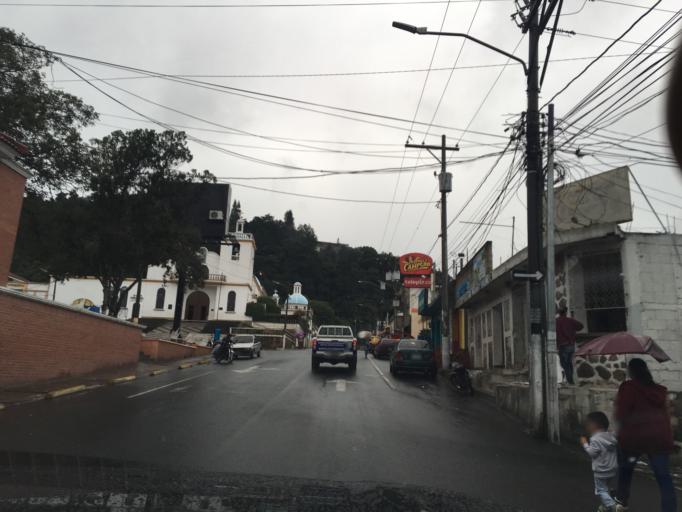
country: GT
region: Guatemala
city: Santa Catarina Pinula
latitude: 14.5704
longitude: -90.4961
